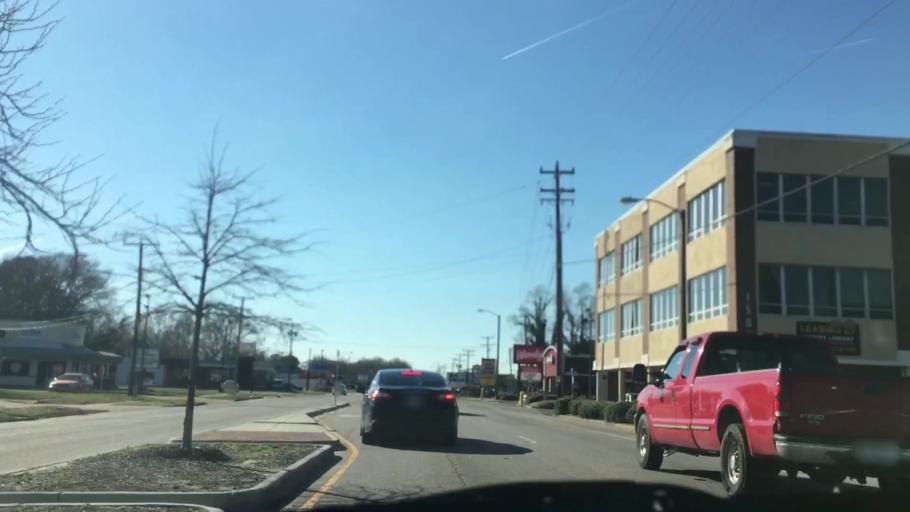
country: US
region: Virginia
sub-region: City of Norfolk
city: Norfolk
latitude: 36.9166
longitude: -76.2330
